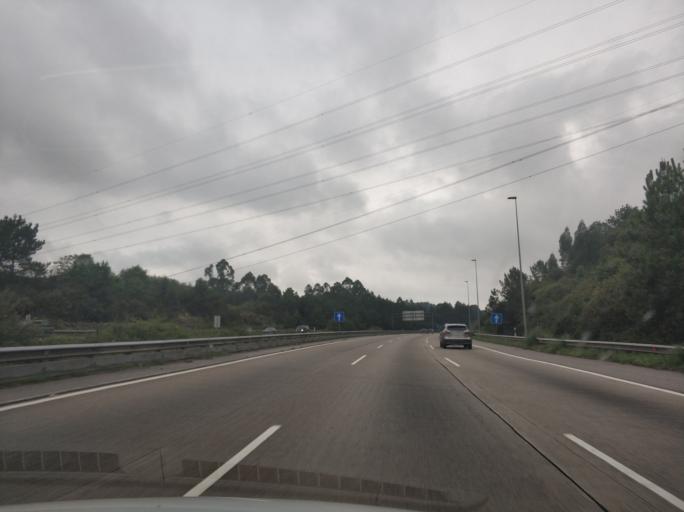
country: ES
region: Asturias
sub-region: Province of Asturias
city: Corvera de Asturias
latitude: 43.5028
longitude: -5.7980
